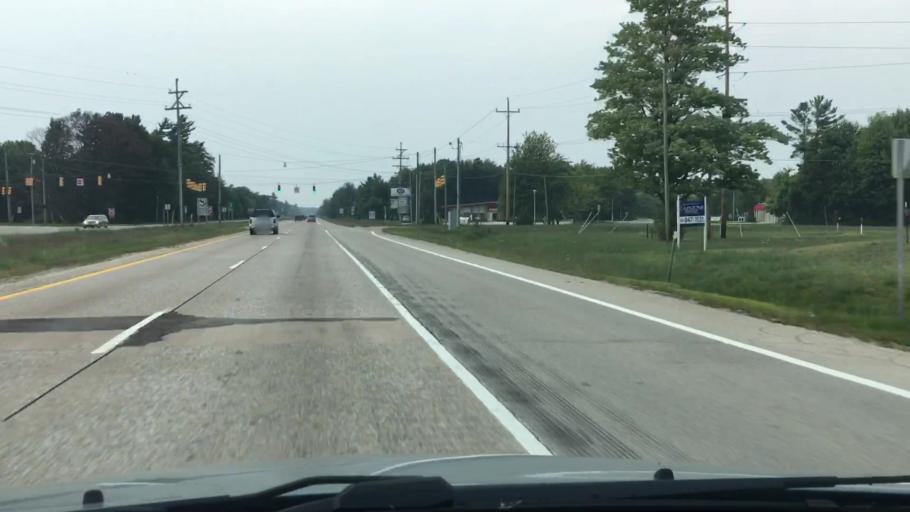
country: US
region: Michigan
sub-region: Ottawa County
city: Grand Haven
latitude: 43.0076
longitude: -86.2046
